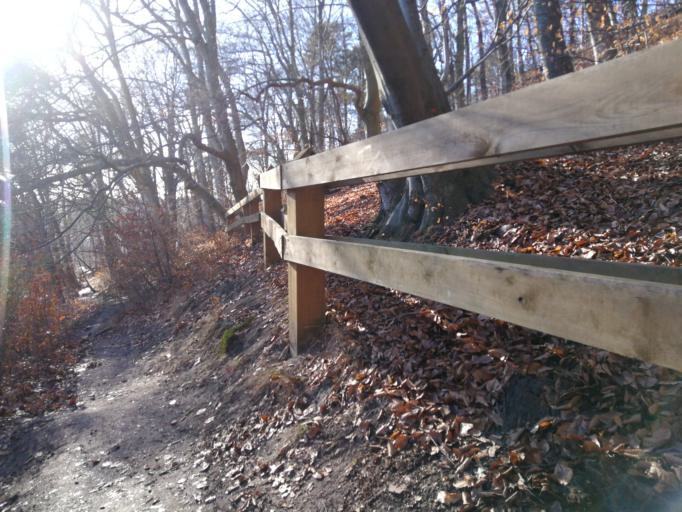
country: PL
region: Pomeranian Voivodeship
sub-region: Sopot
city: Sopot
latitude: 54.4828
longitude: 18.5640
